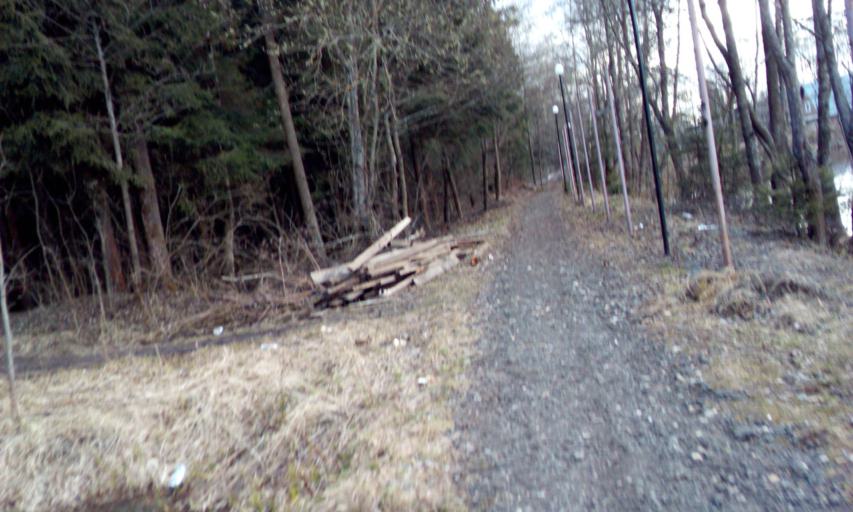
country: RU
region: Moskovskaya
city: Zhavoronki
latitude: 55.6406
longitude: 37.1433
